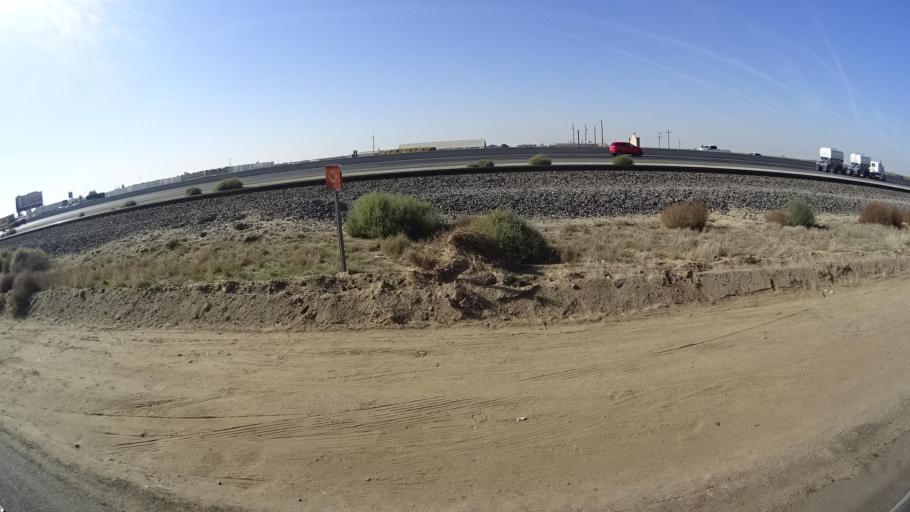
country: US
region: California
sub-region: Kern County
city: McFarland
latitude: 35.6923
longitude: -119.2299
